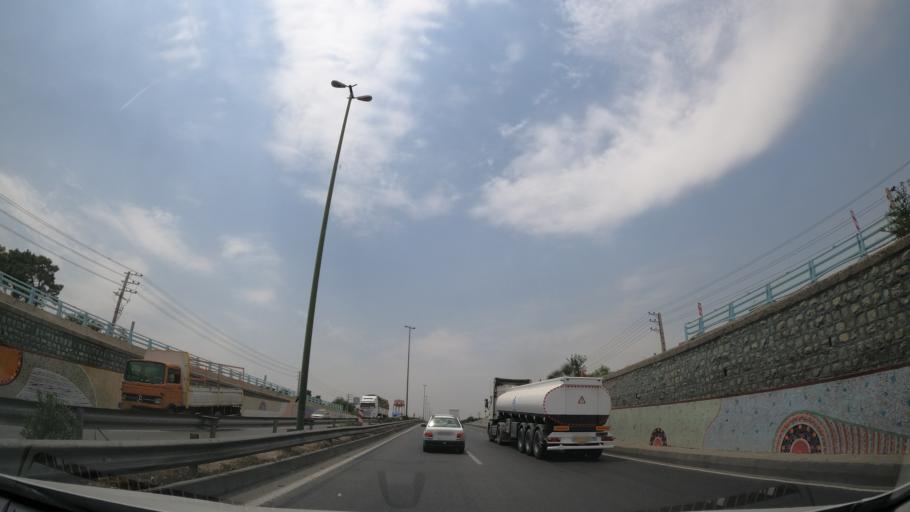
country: IR
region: Tehran
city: Shahr-e Qods
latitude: 35.6925
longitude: 51.2109
